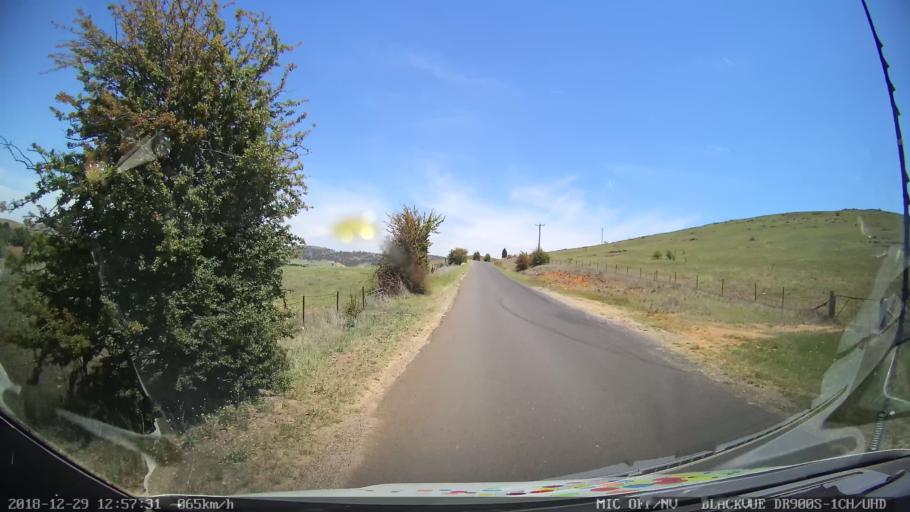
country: AU
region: Australian Capital Territory
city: Macarthur
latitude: -35.7086
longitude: 149.1767
